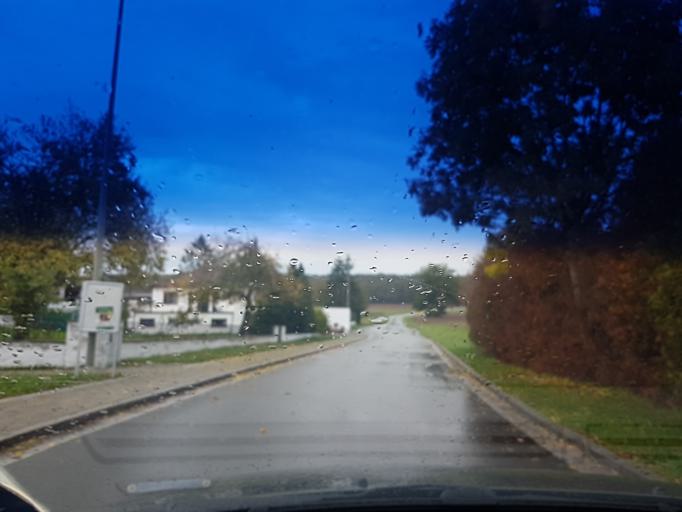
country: DE
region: Bavaria
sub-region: Regierungsbezirk Mittelfranken
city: Wachenroth
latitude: 49.7526
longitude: 10.6667
